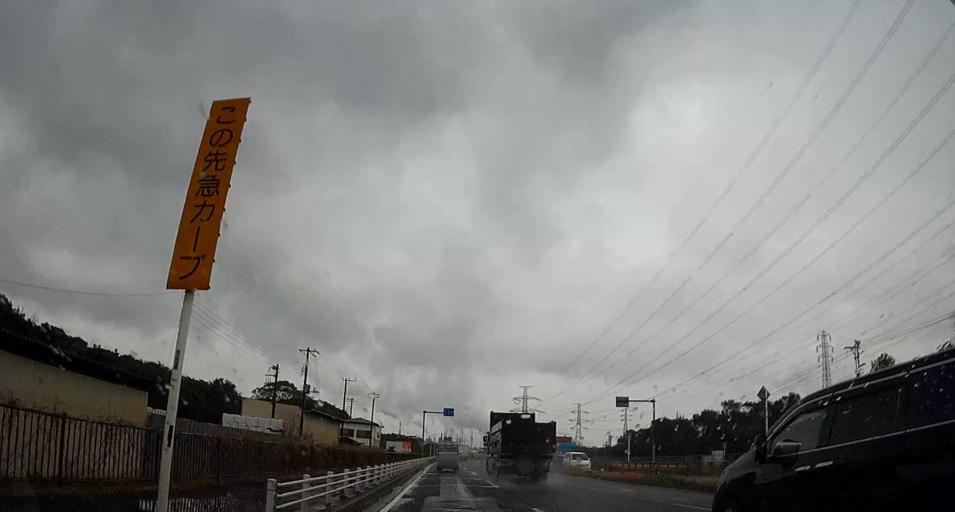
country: JP
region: Chiba
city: Ichihara
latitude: 35.5324
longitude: 140.0825
